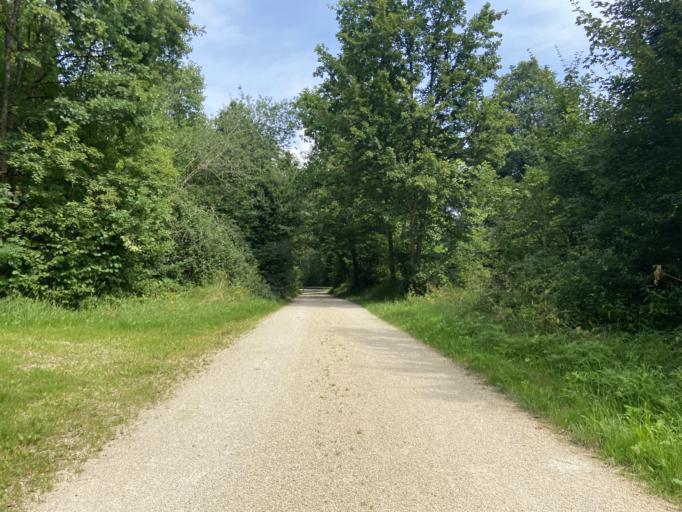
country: DE
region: Baden-Wuerttemberg
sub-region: Tuebingen Region
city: Sigmaringen
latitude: 48.1035
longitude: 9.2342
